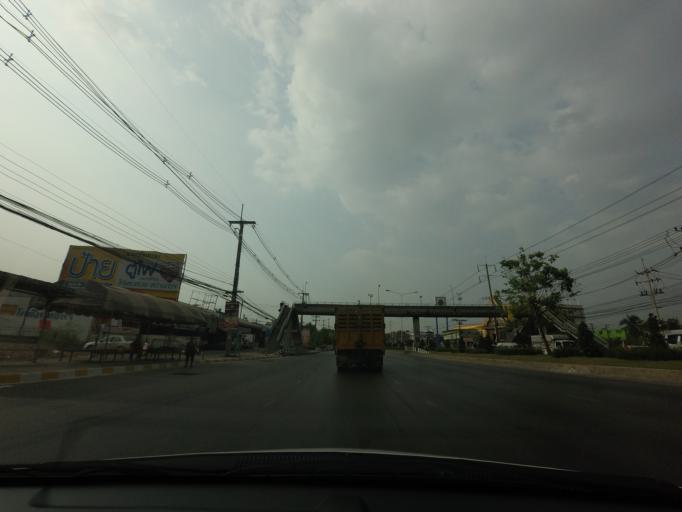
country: TH
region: Bangkok
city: Thawi Watthana
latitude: 13.7467
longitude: 100.3293
